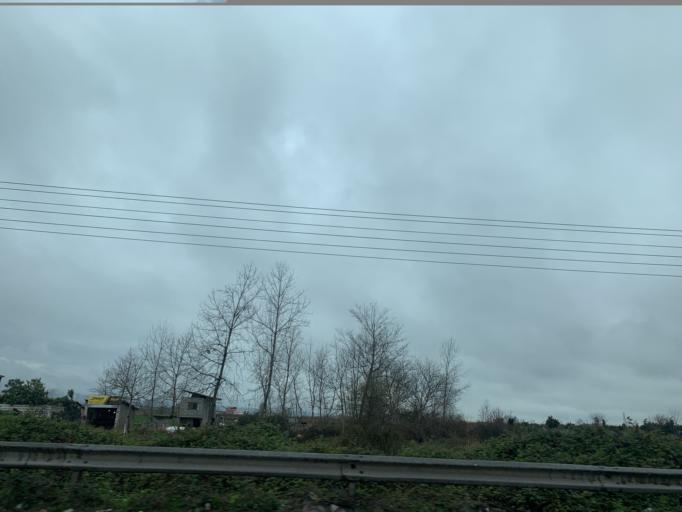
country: IR
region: Mazandaran
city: Amol
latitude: 36.4192
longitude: 52.3494
